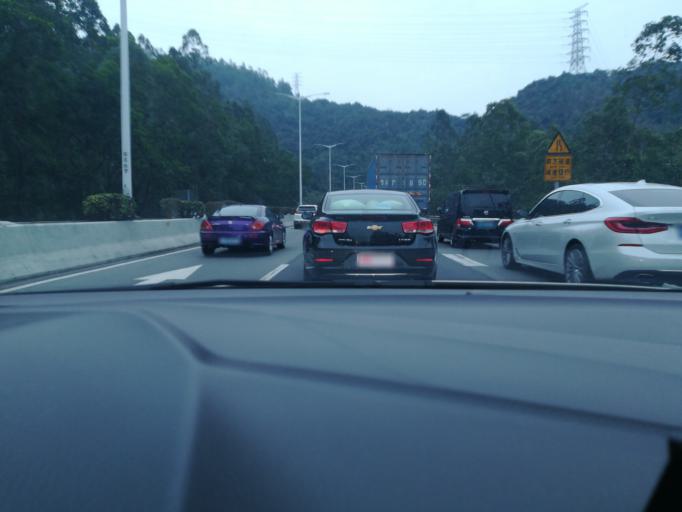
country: CN
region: Guangdong
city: Longdong
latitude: 23.2261
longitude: 113.3562
